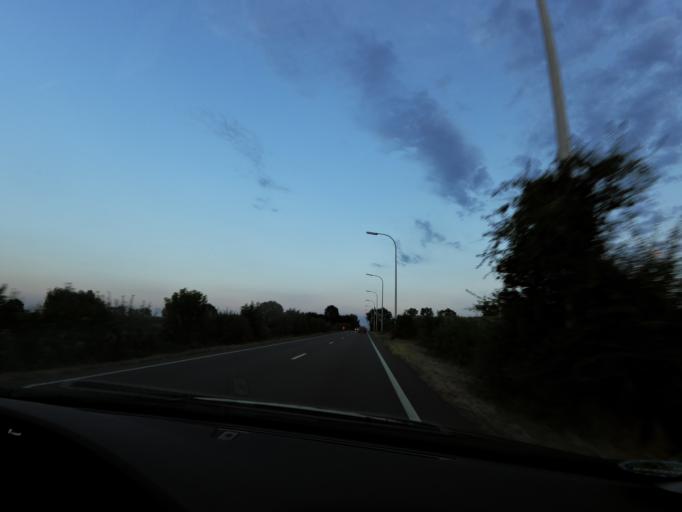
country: BE
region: Wallonia
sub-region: Province de Liege
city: Welkenraedt
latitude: 50.6810
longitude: 5.9597
